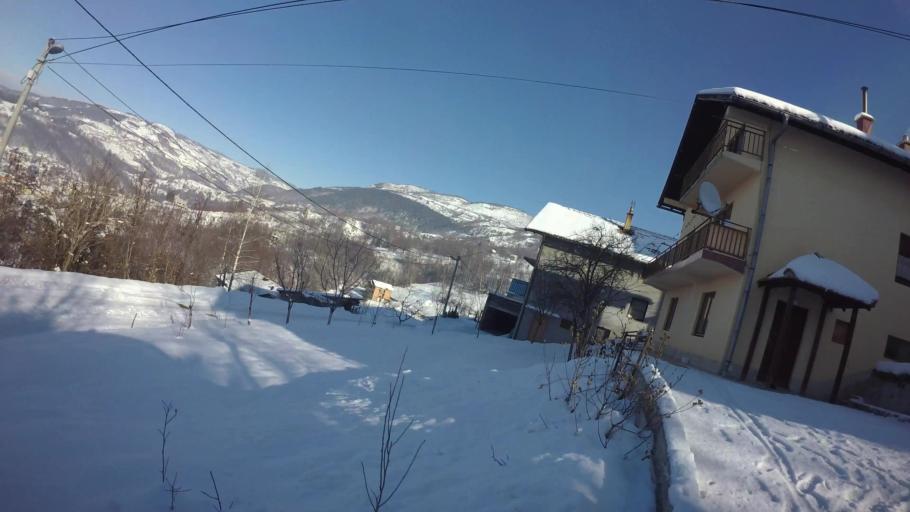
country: BA
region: Federation of Bosnia and Herzegovina
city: Kobilja Glava
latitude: 43.8791
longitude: 18.4221
